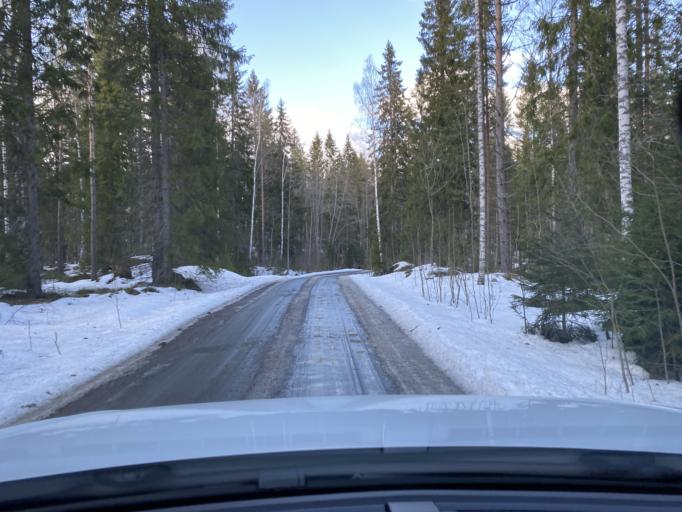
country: FI
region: Pirkanmaa
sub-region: Lounais-Pirkanmaa
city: Mouhijaervi
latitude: 61.4514
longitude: 22.9208
